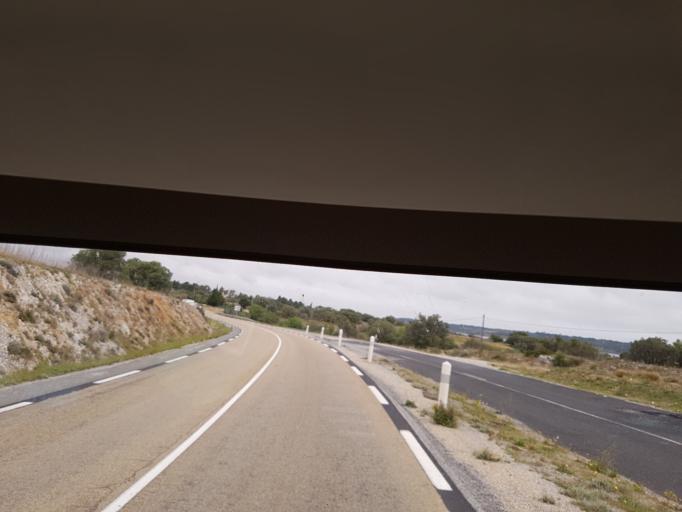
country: FR
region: Languedoc-Roussillon
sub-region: Departement de l'Aude
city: Leucate
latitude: 42.9020
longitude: 3.0009
